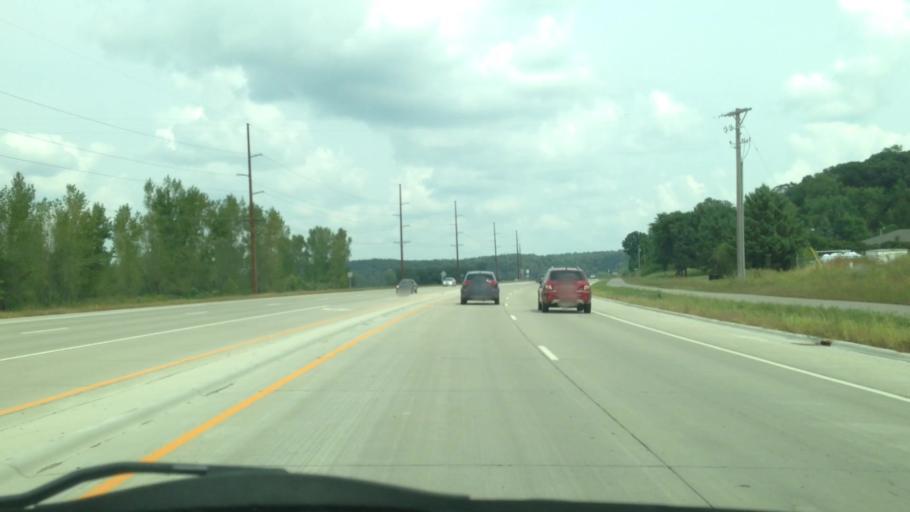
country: US
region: Minnesota
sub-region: Olmsted County
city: Rochester
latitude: 44.0629
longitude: -92.4525
